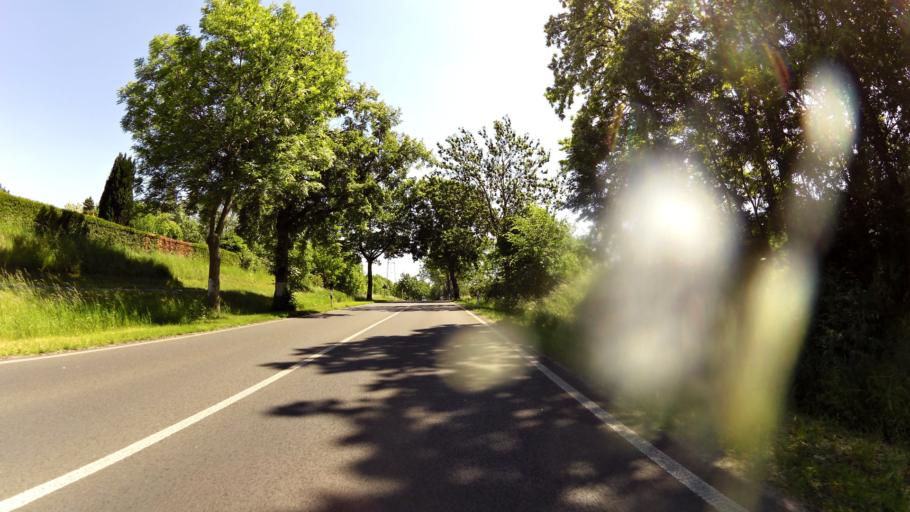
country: DE
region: Brandenburg
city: Frankfurt (Oder)
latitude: 52.3692
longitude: 14.5245
